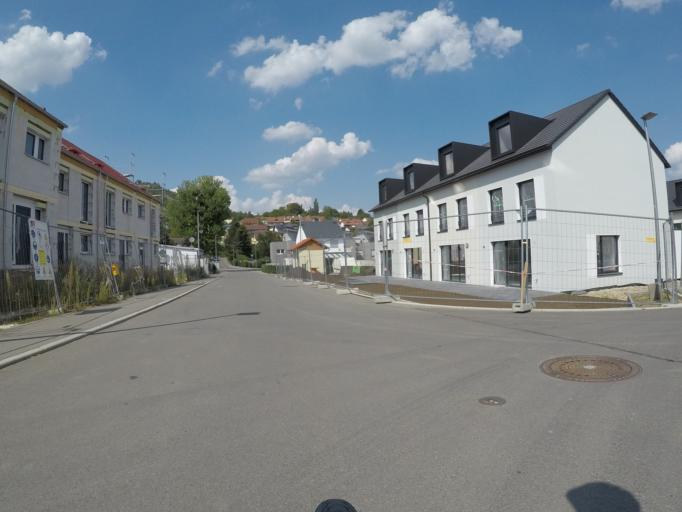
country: DE
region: Baden-Wuerttemberg
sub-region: Tuebingen Region
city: Eningen unter Achalm
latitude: 48.4836
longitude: 9.2491
